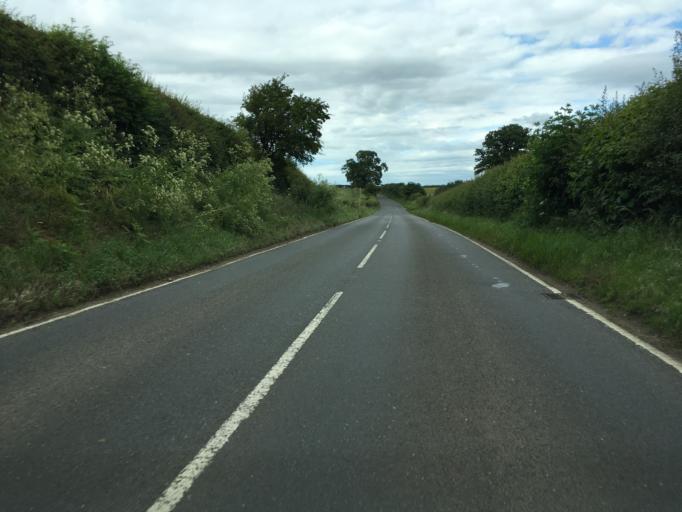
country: GB
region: England
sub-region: Central Bedfordshire
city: Woburn
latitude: 51.9760
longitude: -0.6396
